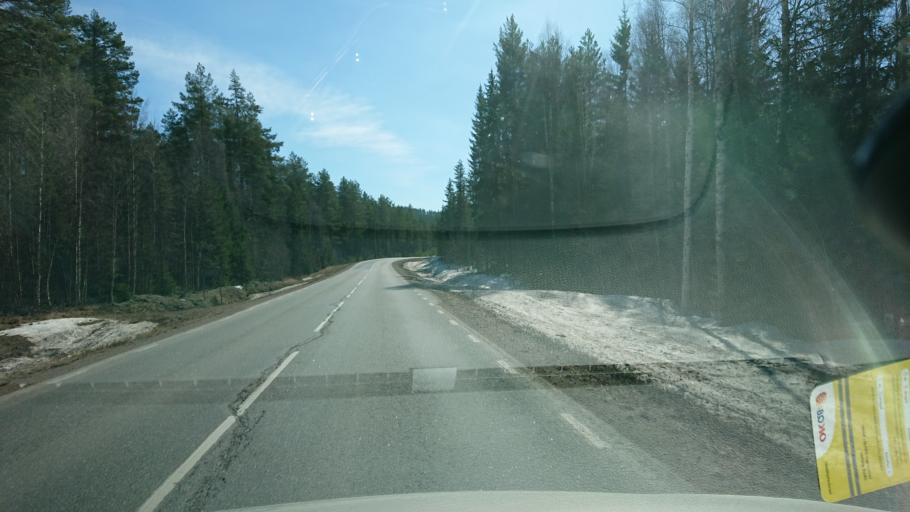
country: SE
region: Vaesternorrland
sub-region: Solleftea Kommun
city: As
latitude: 63.5697
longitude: 16.4516
